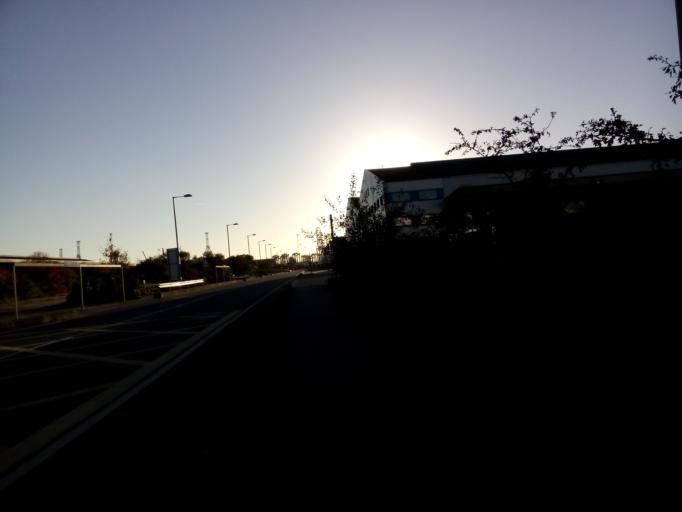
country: GB
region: England
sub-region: Suffolk
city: Felixstowe
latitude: 51.9646
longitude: 1.3162
